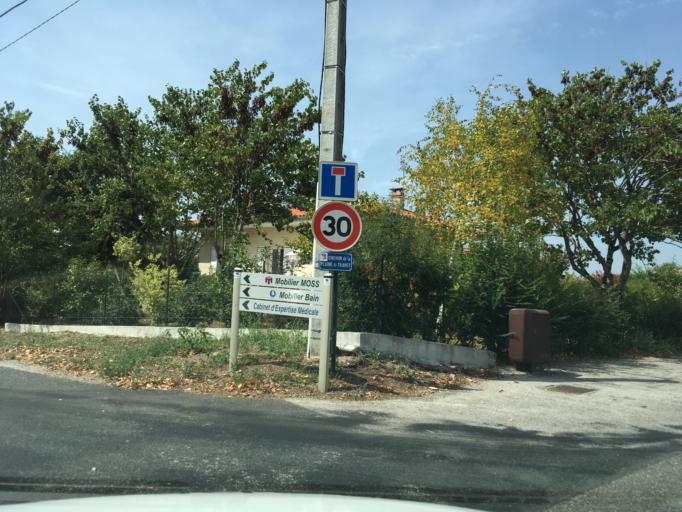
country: FR
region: Midi-Pyrenees
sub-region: Departement du Tarn
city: Castres
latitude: 43.6164
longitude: 2.2297
